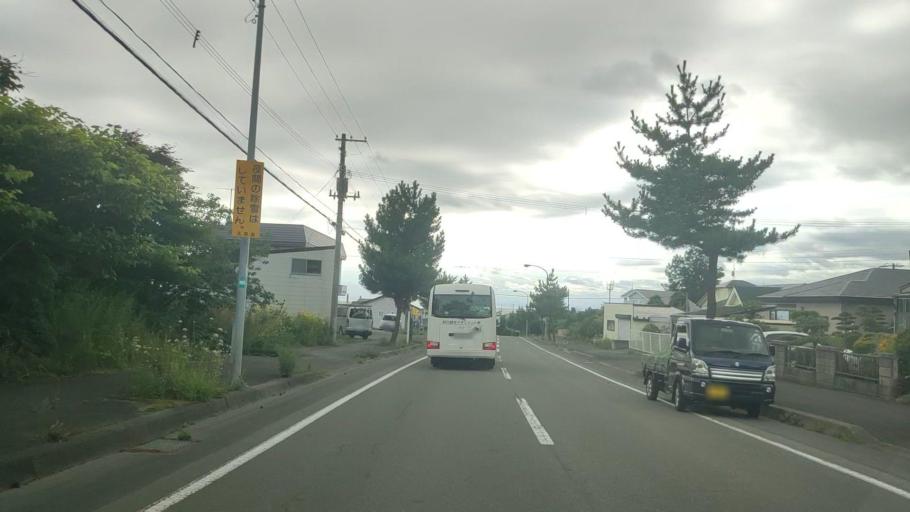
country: JP
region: Hokkaido
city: Date
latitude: 42.5486
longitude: 140.7704
